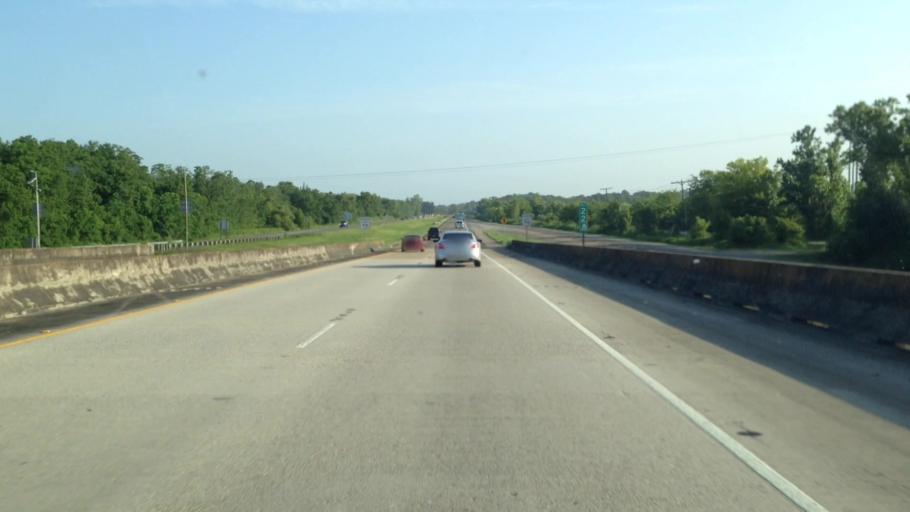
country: US
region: Louisiana
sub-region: Tangipahoa Parish
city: Ponchatoula
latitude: 30.4001
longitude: -90.4305
